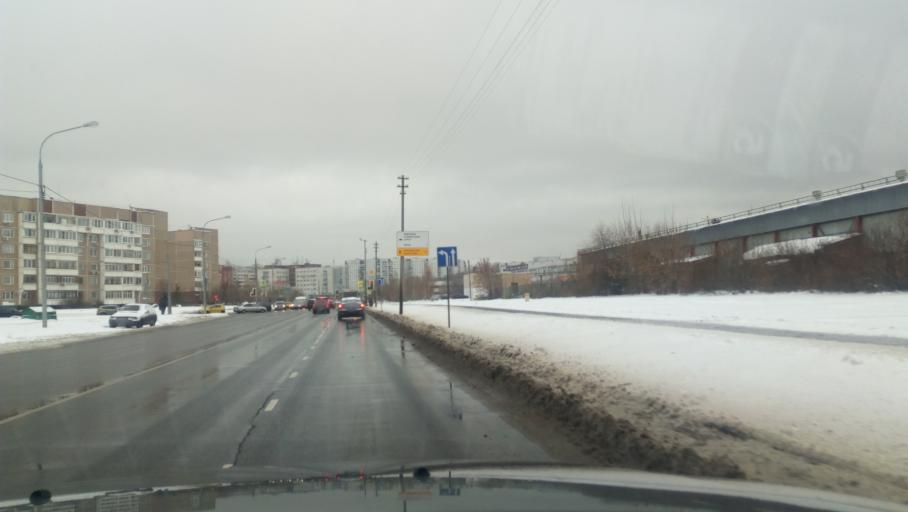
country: RU
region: Moskovskaya
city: Reutov
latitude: 55.7297
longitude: 37.8607
